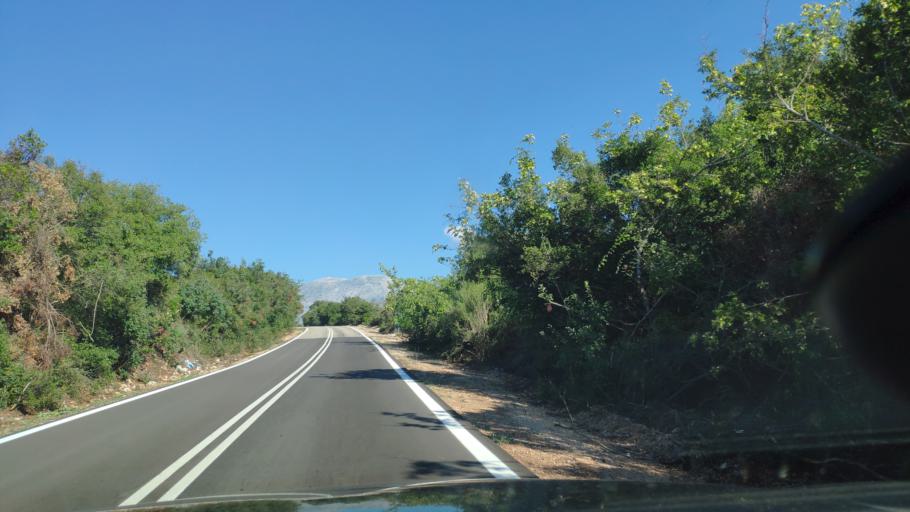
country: GR
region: West Greece
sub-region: Nomos Aitolias kai Akarnanias
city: Fitiai
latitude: 38.6820
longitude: 21.1282
